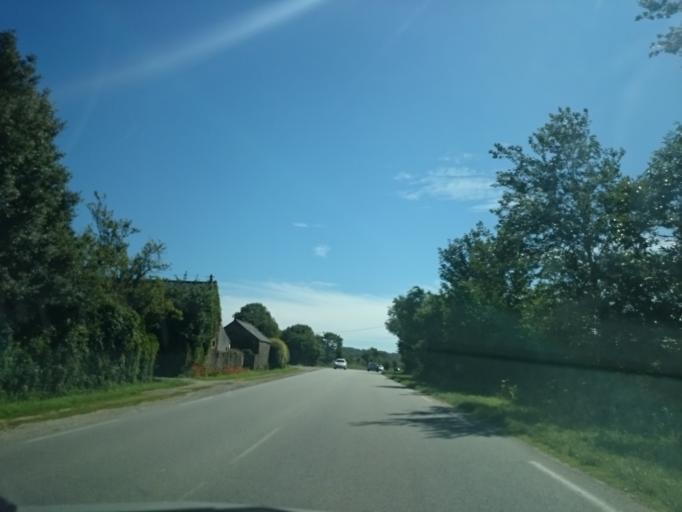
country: FR
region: Brittany
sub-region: Departement du Finistere
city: Saint-Renan
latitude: 48.4314
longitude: -4.6075
